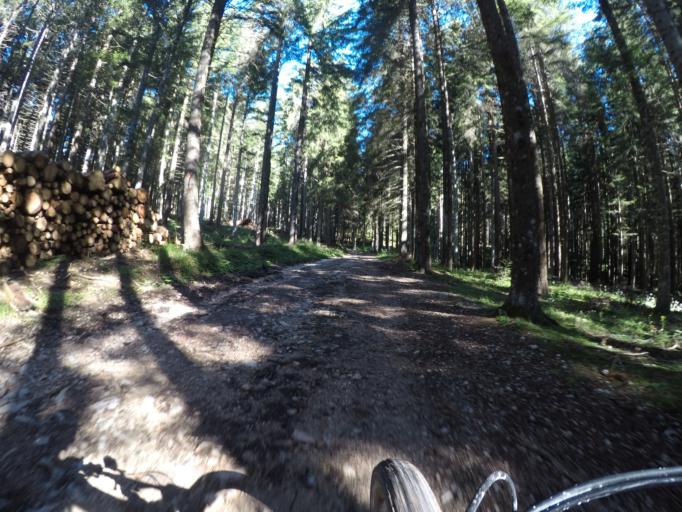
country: IT
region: Veneto
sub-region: Provincia di Vicenza
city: Asiago
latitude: 45.9045
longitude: 11.4838
